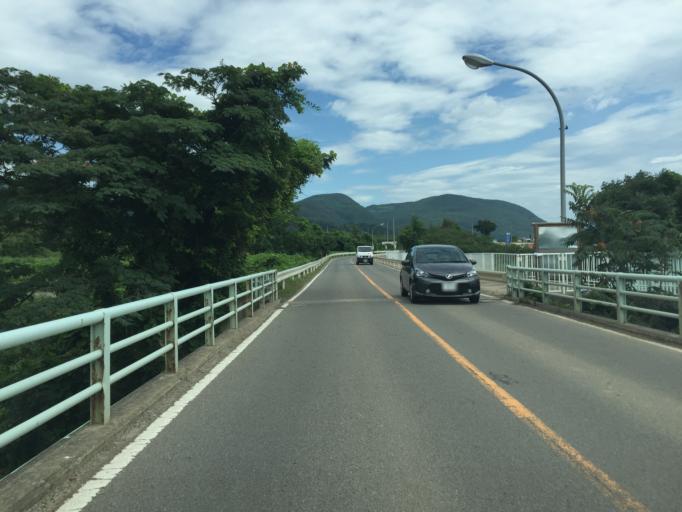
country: JP
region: Fukushima
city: Fukushima-shi
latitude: 37.7849
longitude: 140.3938
